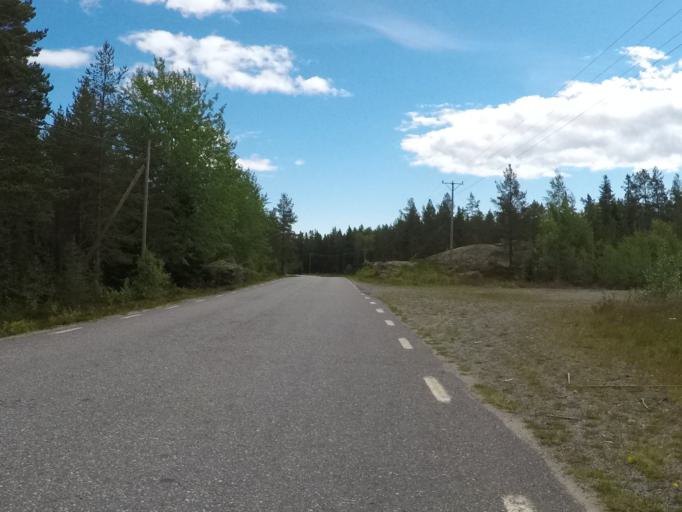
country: SE
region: Vaesterbotten
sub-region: Robertsfors Kommun
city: Robertsfors
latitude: 63.9903
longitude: 20.8248
